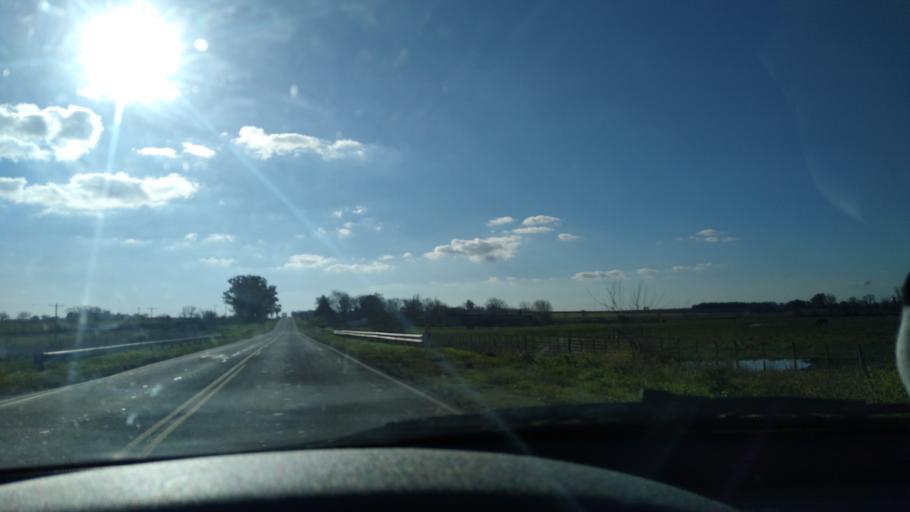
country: AR
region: Entre Rios
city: Diamante
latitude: -32.1158
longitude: -60.5722
